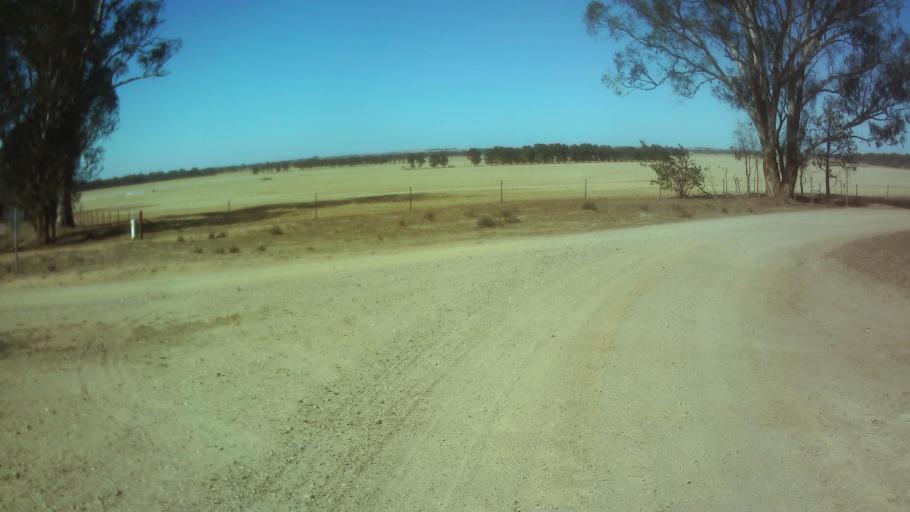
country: AU
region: New South Wales
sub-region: Weddin
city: Grenfell
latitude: -33.9906
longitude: 148.3391
